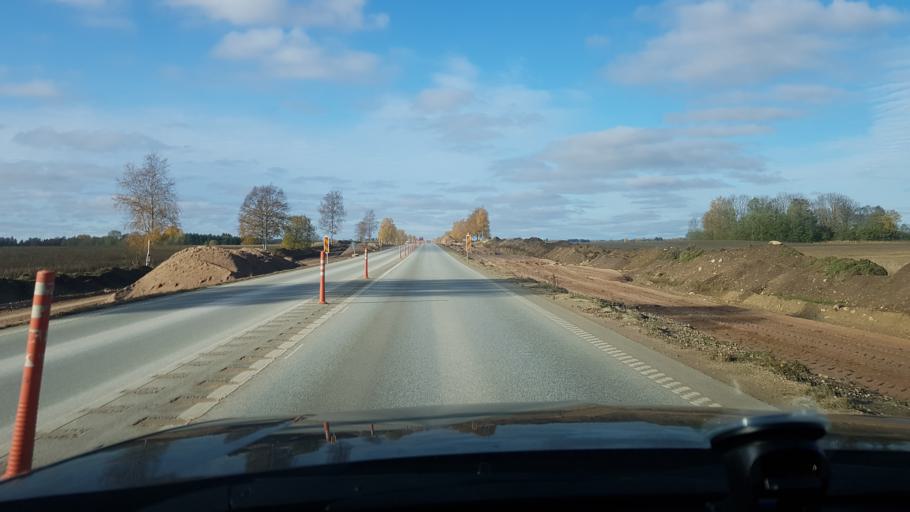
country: EE
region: Laeaene-Virumaa
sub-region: Haljala vald
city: Haljala
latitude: 59.4282
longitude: 26.2319
